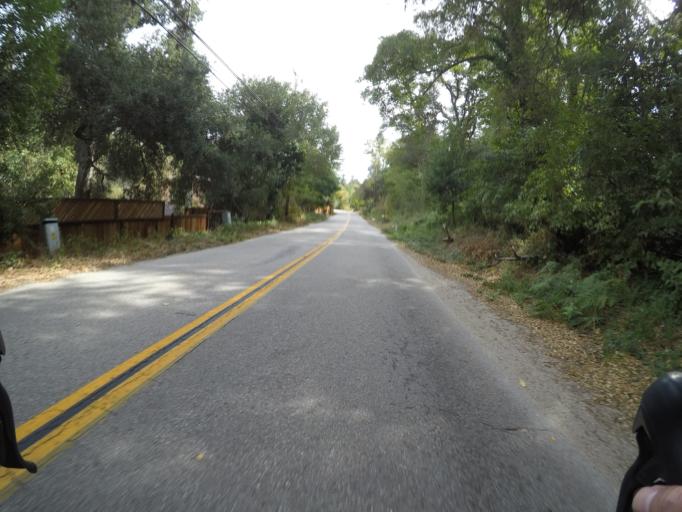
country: US
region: California
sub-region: Santa Cruz County
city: Mount Hermon
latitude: 37.0643
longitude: -122.0573
